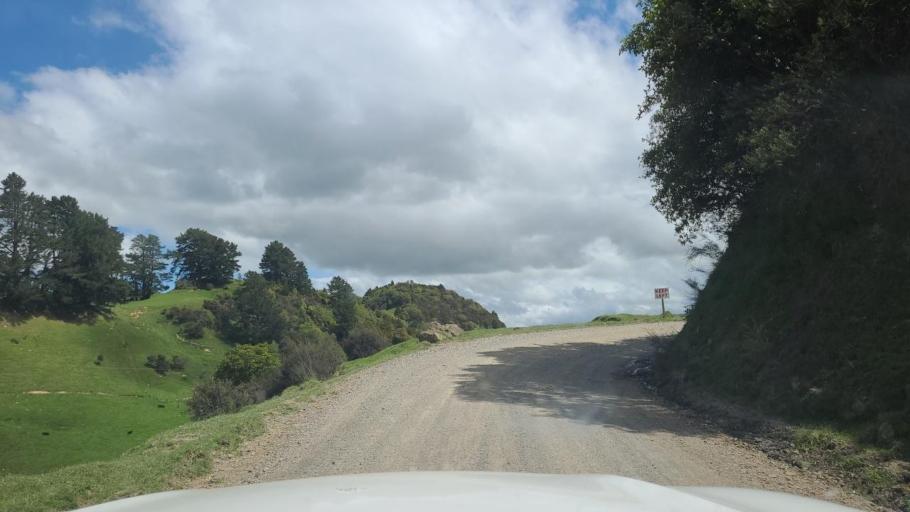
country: NZ
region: Hawke's Bay
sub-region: Napier City
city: Taradale
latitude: -39.2683
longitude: 176.6612
